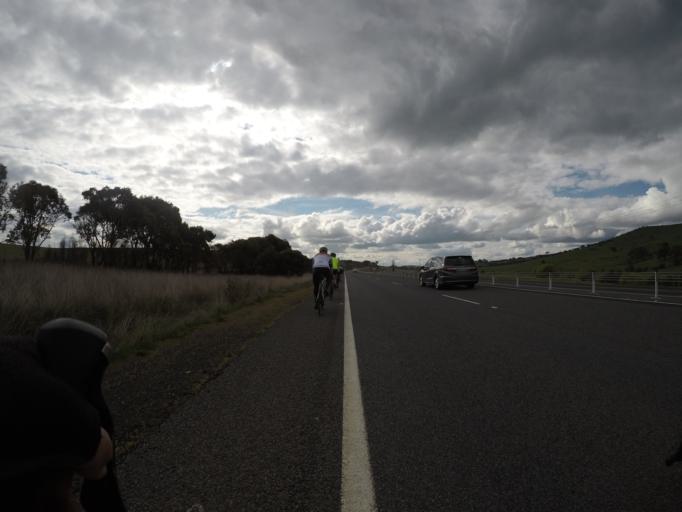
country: AU
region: New South Wales
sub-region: Blayney
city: Millthorpe
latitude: -33.3647
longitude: 149.1804
